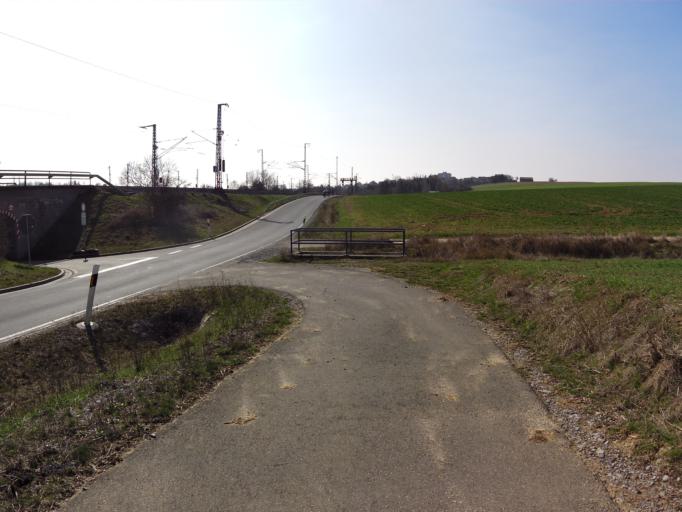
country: DE
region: Bavaria
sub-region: Regierungsbezirk Unterfranken
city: Rottendorf
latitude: 49.8016
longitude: 10.0384
